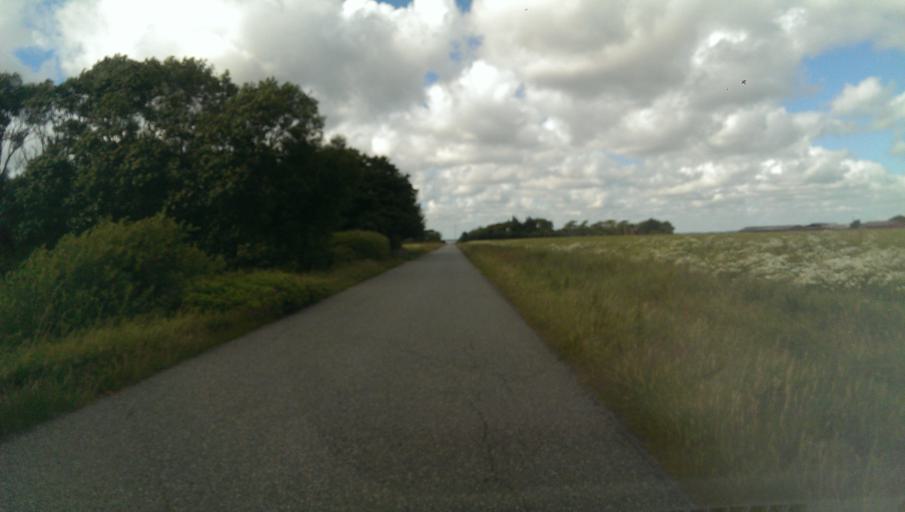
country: DK
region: Central Jutland
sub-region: Holstebro Kommune
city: Ulfborg
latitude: 56.2722
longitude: 8.2475
